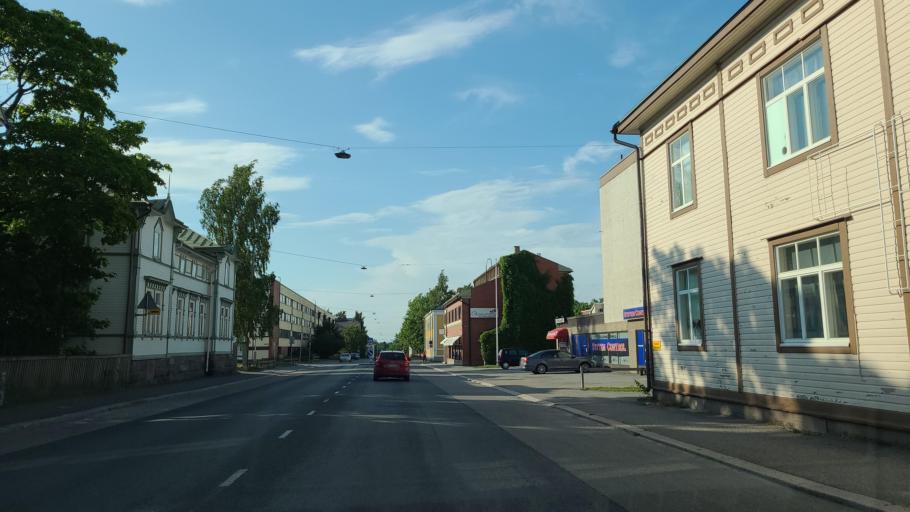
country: FI
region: Ostrobothnia
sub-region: Vaasa
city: Vaasa
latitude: 63.1015
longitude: 21.6207
